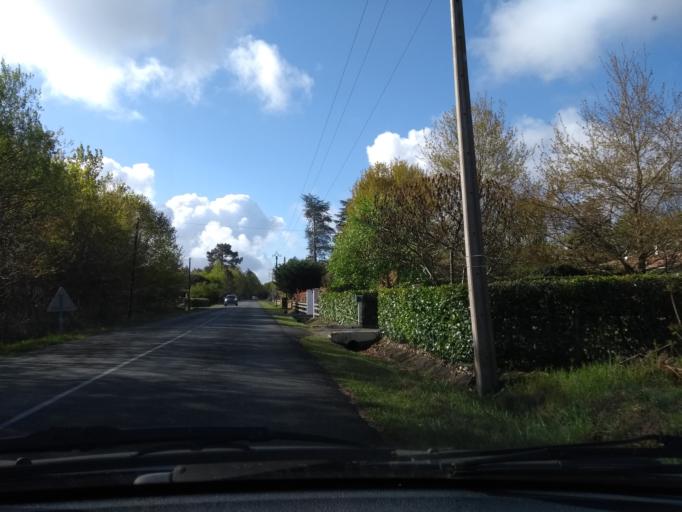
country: FR
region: Aquitaine
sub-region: Departement des Landes
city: Sanguinet
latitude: 44.4714
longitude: -1.0698
